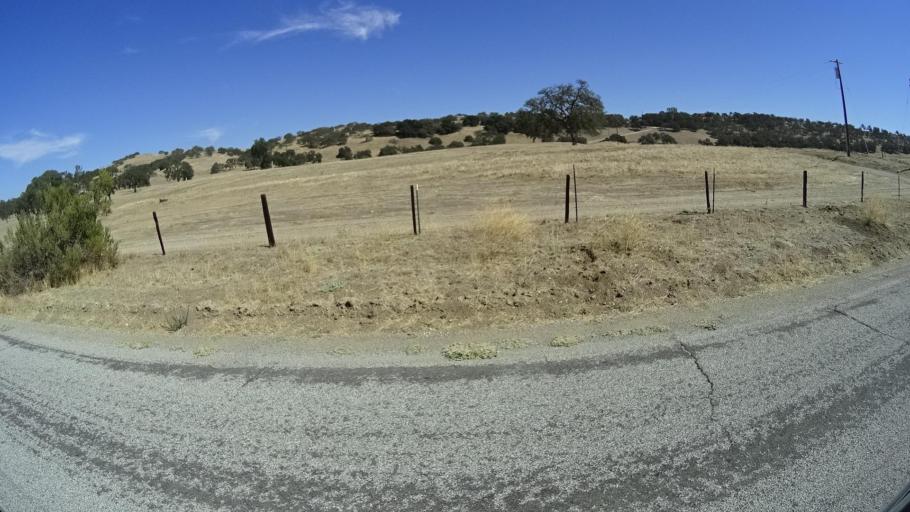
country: US
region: California
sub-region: San Luis Obispo County
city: San Miguel
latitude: 35.8503
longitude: -120.7005
